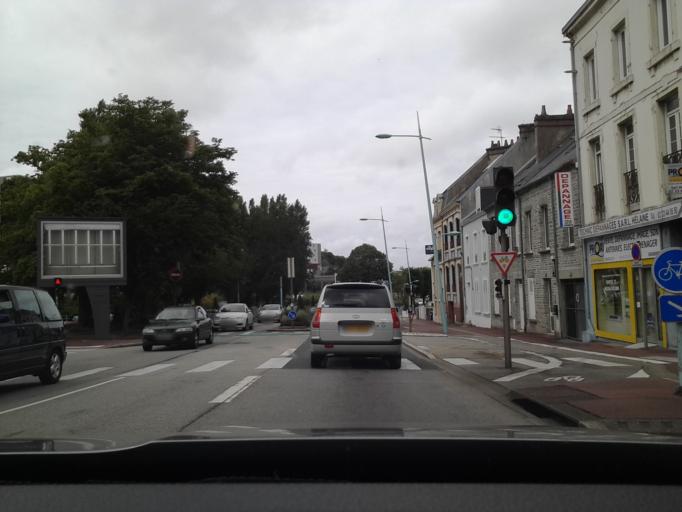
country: FR
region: Lower Normandy
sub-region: Departement de la Manche
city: Cherbourg-Octeville
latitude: 49.6277
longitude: -1.6179
